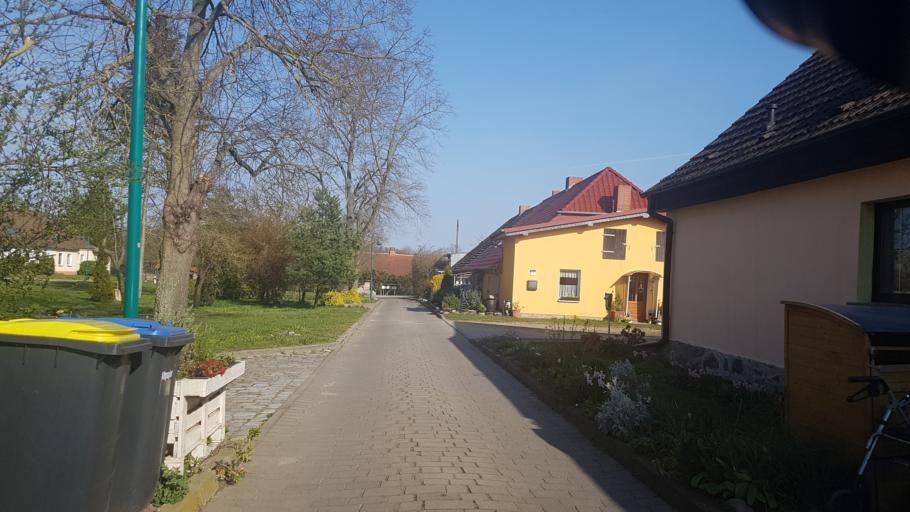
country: DE
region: Brandenburg
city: Prenzlau
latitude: 53.2278
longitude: 13.8434
